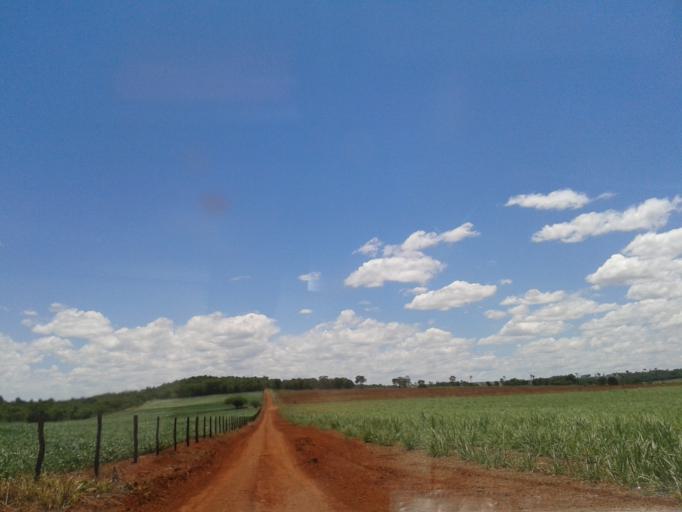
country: BR
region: Minas Gerais
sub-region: Centralina
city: Centralina
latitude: -18.6752
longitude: -49.2290
